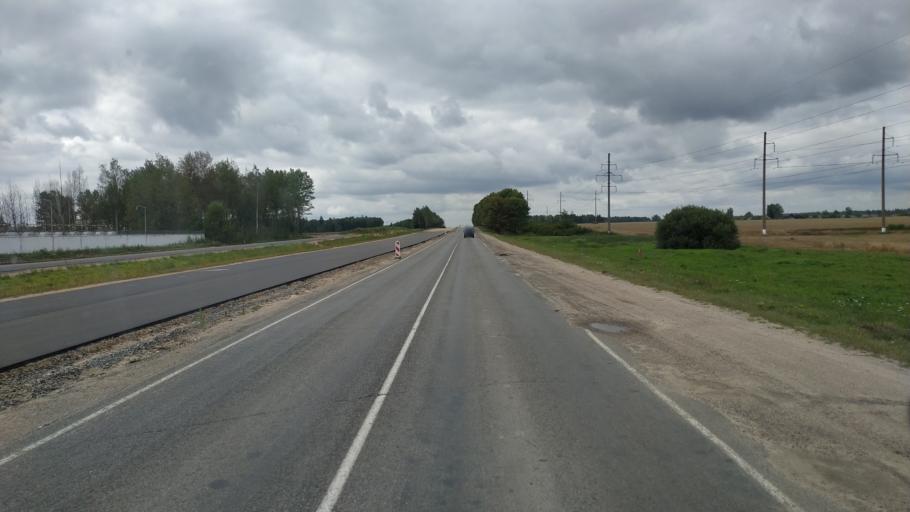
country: BY
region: Mogilev
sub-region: Mahilyowski Rayon
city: Kadino
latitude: 53.8689
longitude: 30.4676
